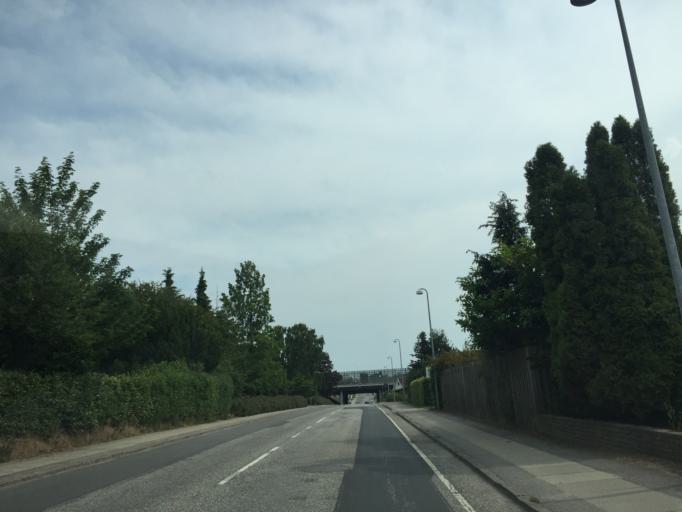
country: DK
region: Capital Region
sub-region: Hoje-Taastrup Kommune
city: Flong
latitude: 55.6581
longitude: 12.1851
